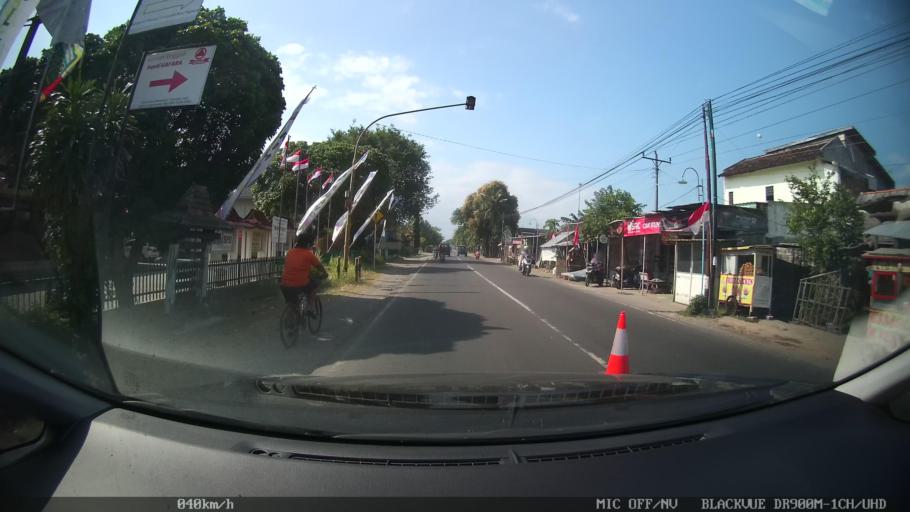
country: ID
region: Daerah Istimewa Yogyakarta
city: Sewon
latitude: -7.8918
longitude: 110.3859
